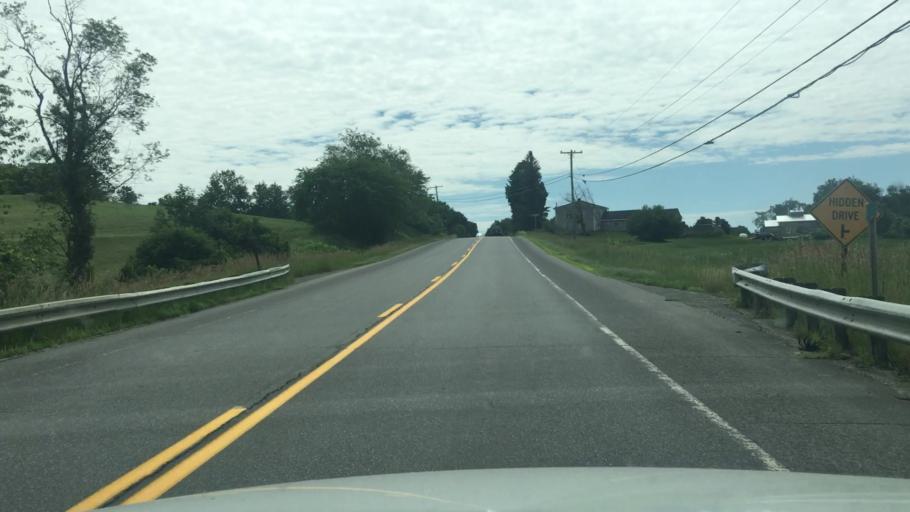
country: US
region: Maine
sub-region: Waldo County
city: Troy
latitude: 44.6058
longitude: -69.2999
